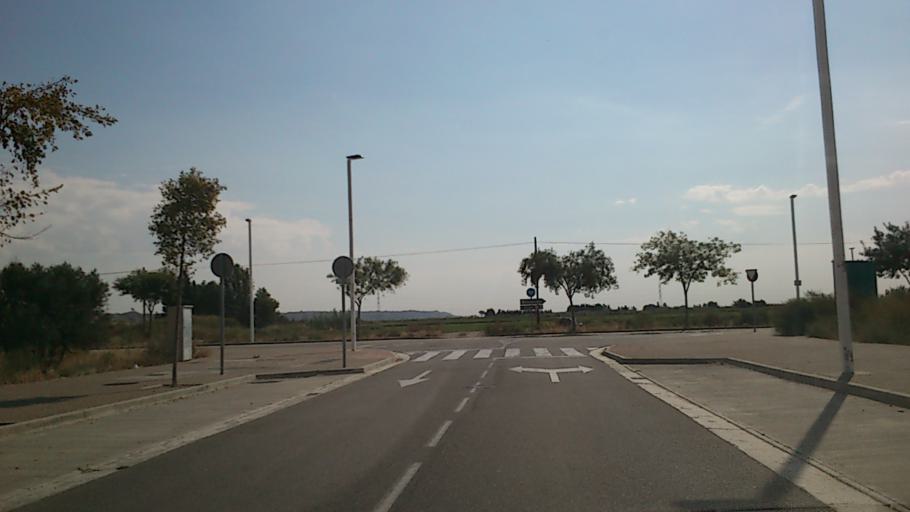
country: ES
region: Aragon
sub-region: Provincia de Zaragoza
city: Puebla de Alfinden
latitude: 41.6284
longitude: -0.7542
